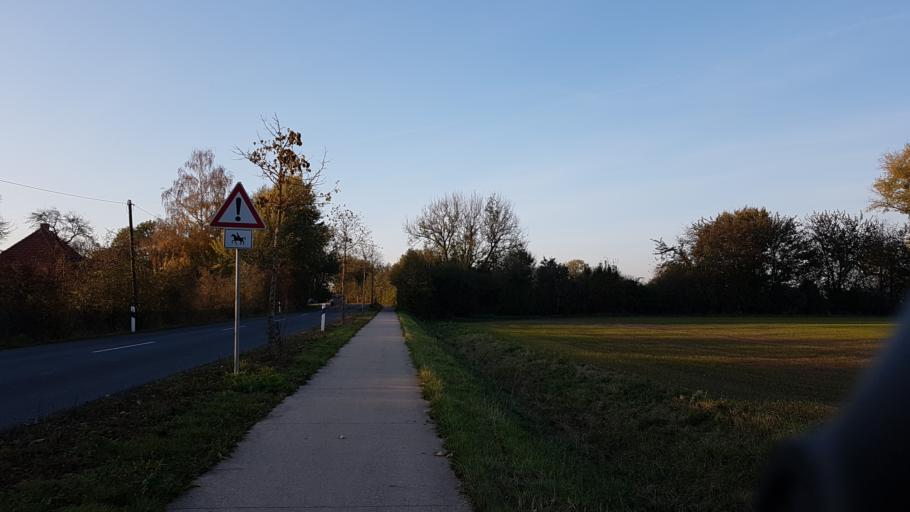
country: DE
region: Lower Saxony
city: Ronnenberg
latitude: 52.2994
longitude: 9.6645
